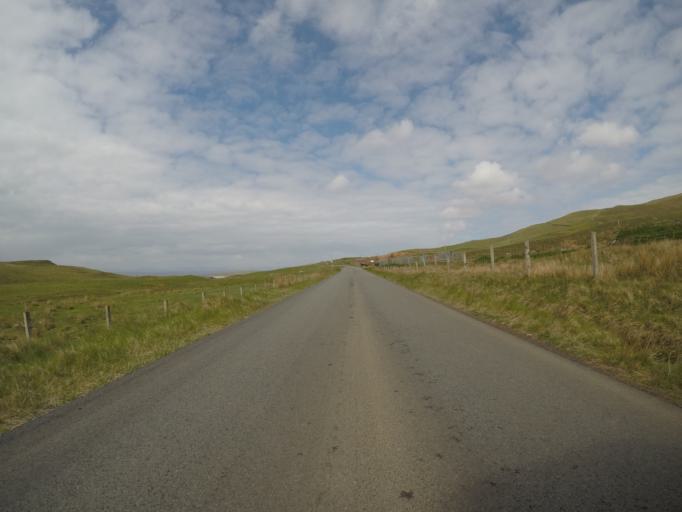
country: GB
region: Scotland
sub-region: Highland
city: Portree
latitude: 57.5982
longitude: -6.3758
